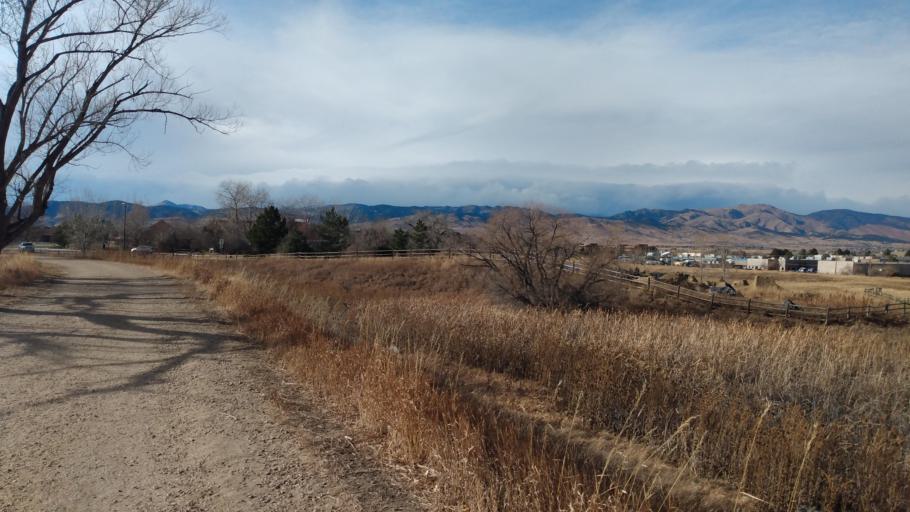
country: US
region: Colorado
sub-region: Boulder County
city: Gunbarrel
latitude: 40.0635
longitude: -105.1990
